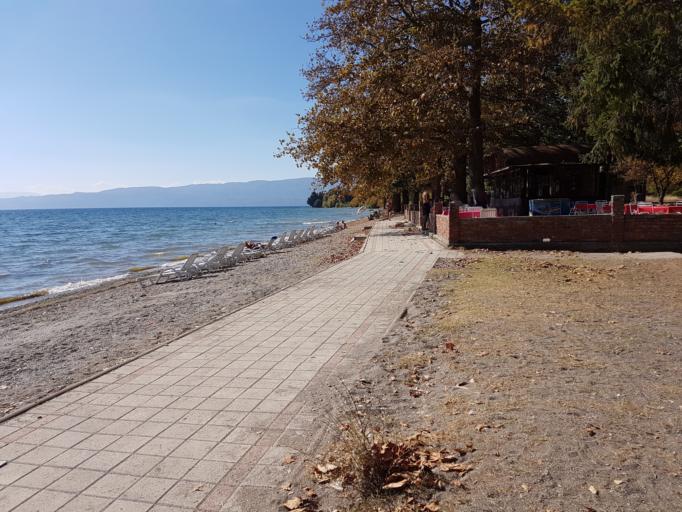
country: MK
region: Ohrid
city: Ohrid
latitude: 41.1204
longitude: 20.7805
